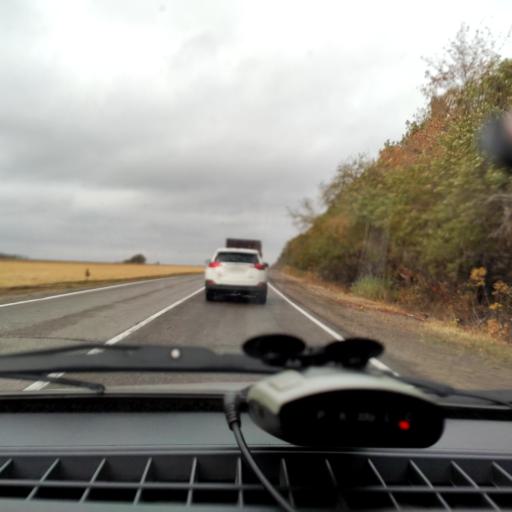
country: RU
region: Voronezj
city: Kolodeznyy
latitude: 51.3815
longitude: 39.0128
